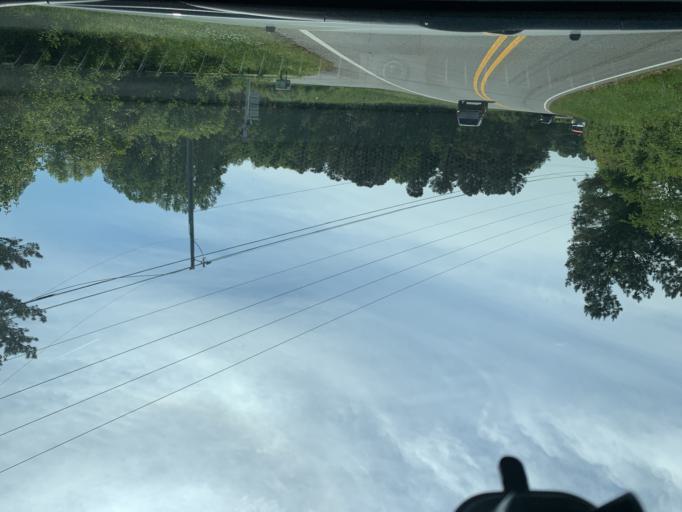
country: US
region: Georgia
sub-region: Forsyth County
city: Cumming
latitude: 34.2811
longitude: -84.1734
